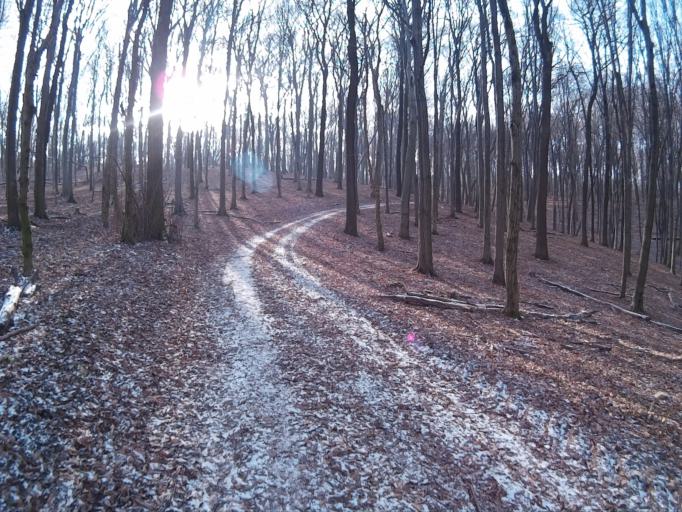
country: HU
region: Fejer
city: Szarliget
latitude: 47.4883
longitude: 18.4097
